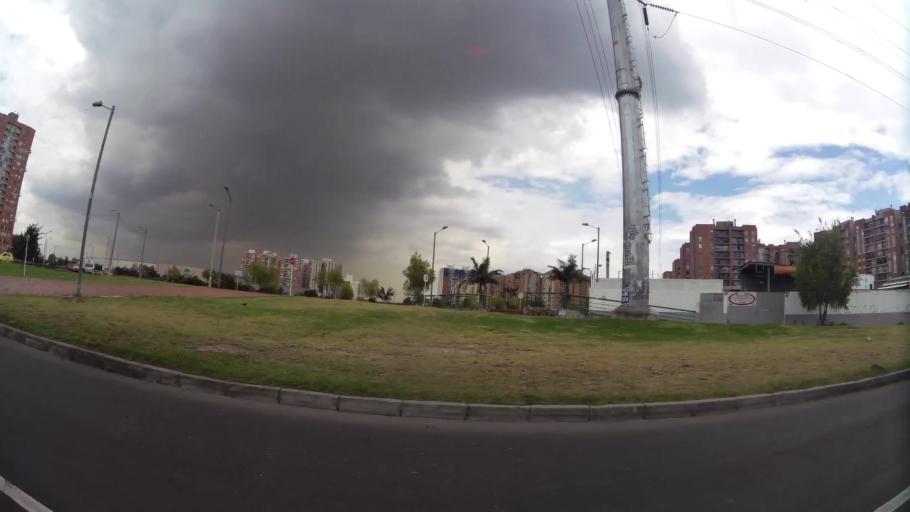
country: CO
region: Bogota D.C.
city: Barrio San Luis
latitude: 4.6908
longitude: -74.0799
